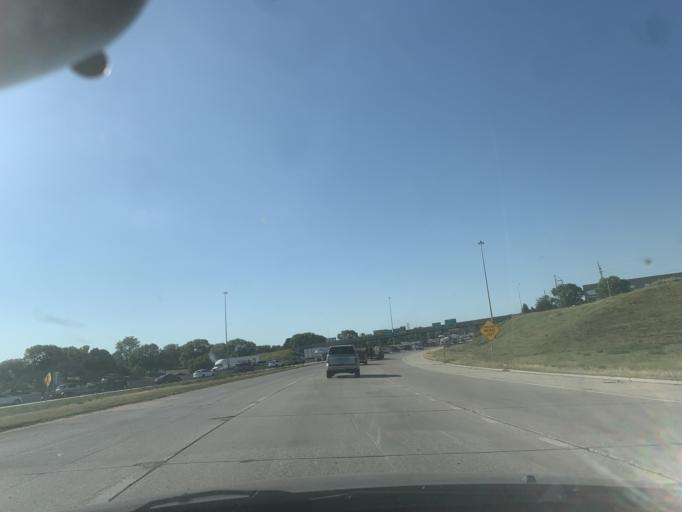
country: US
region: Nebraska
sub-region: Douglas County
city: Ralston
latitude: 41.2141
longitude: -96.0897
